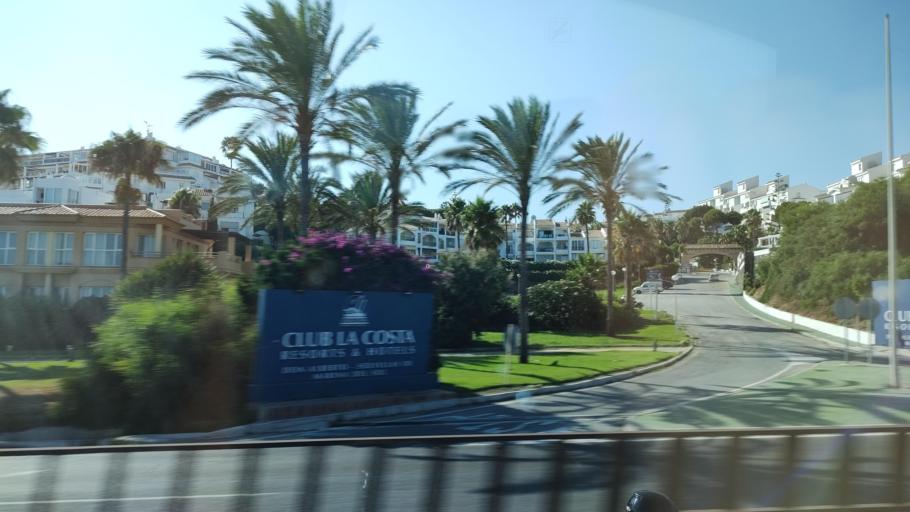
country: ES
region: Andalusia
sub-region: Provincia de Malaga
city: Fuengirola
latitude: 36.5151
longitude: -4.6329
